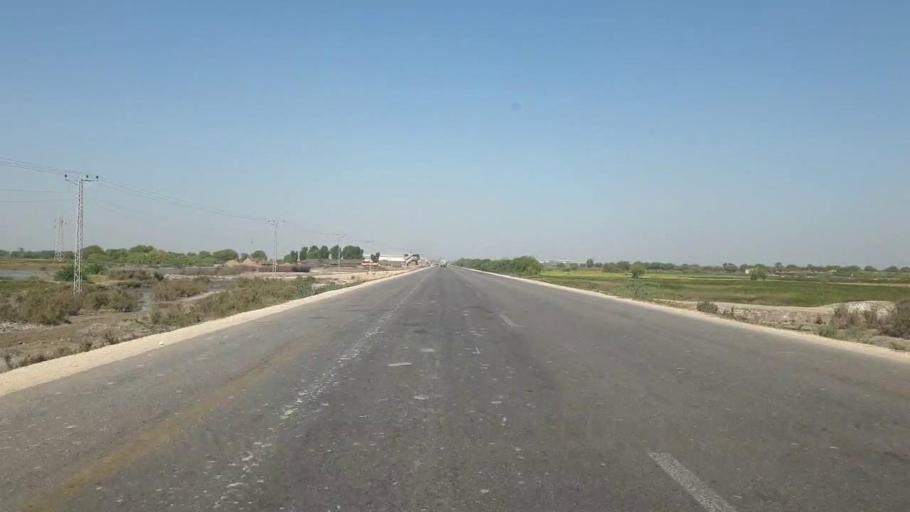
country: PK
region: Sindh
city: Talhar
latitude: 24.8586
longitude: 68.8165
